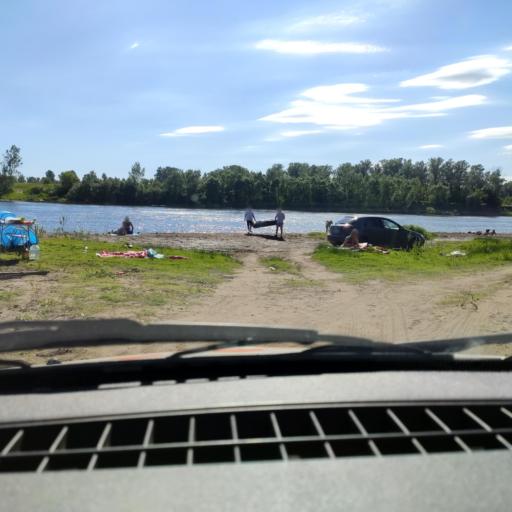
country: RU
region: Bashkortostan
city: Iglino
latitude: 54.8016
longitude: 56.2214
